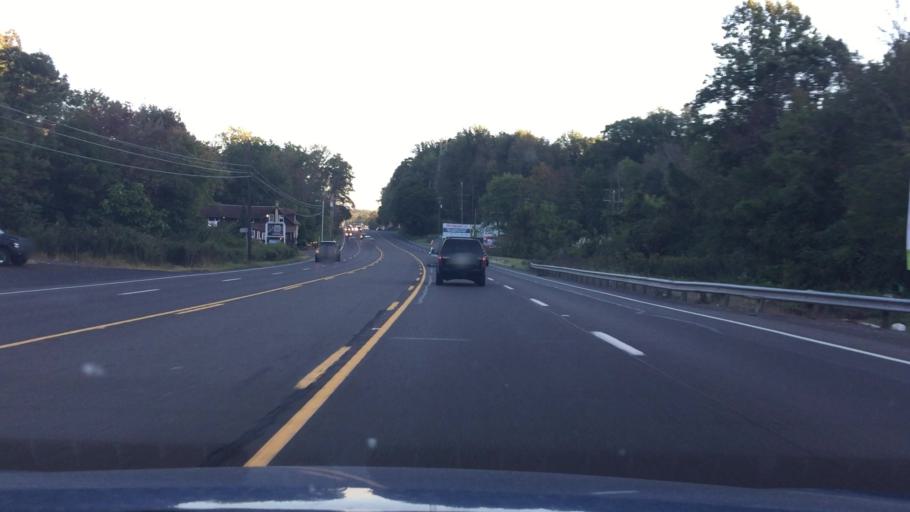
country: US
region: Pennsylvania
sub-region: Lehigh County
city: Coopersburg
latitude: 40.4866
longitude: -75.3783
